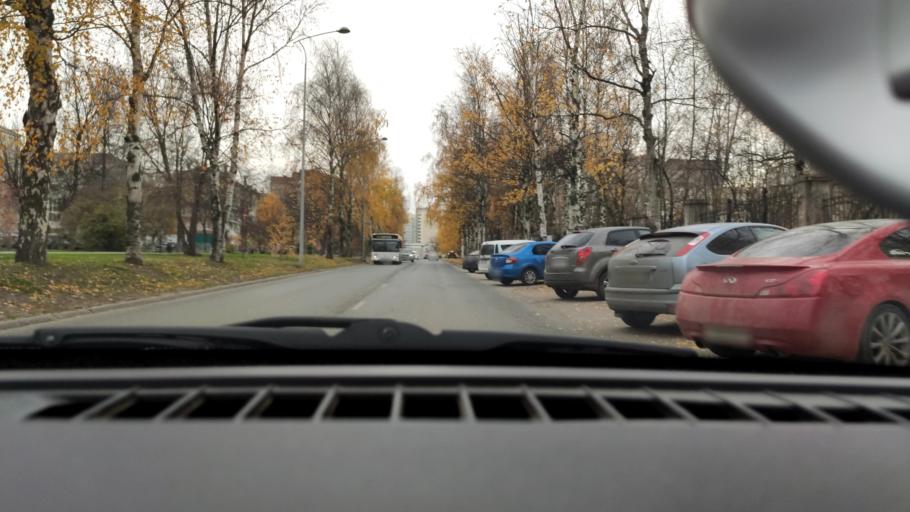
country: RU
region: Perm
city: Perm
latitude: 57.9803
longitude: 56.1820
